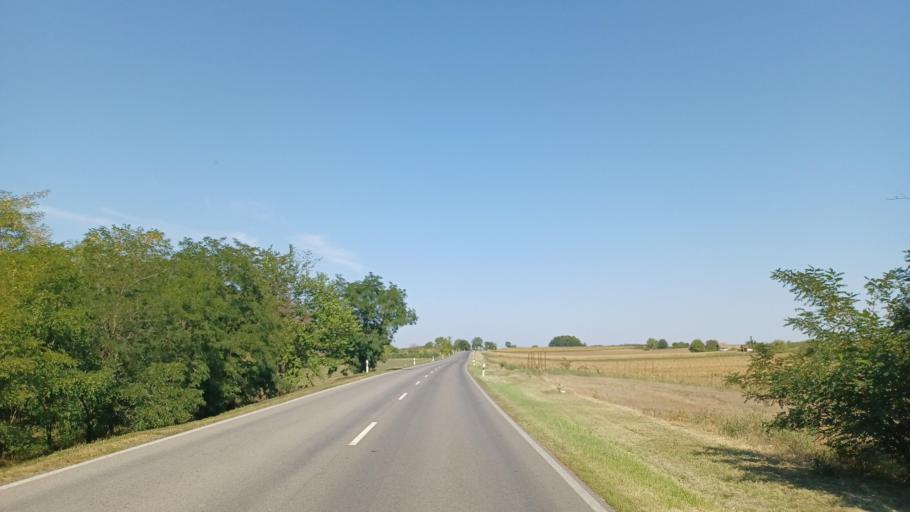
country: HU
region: Tolna
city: Nagydorog
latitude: 46.6399
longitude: 18.6508
